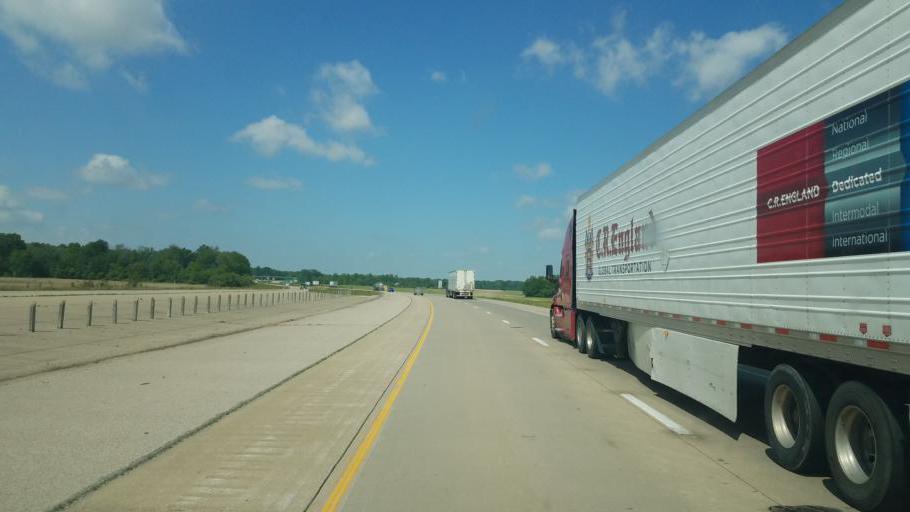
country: US
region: Indiana
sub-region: Vigo County
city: West Terre Haute
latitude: 39.4296
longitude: -87.5681
